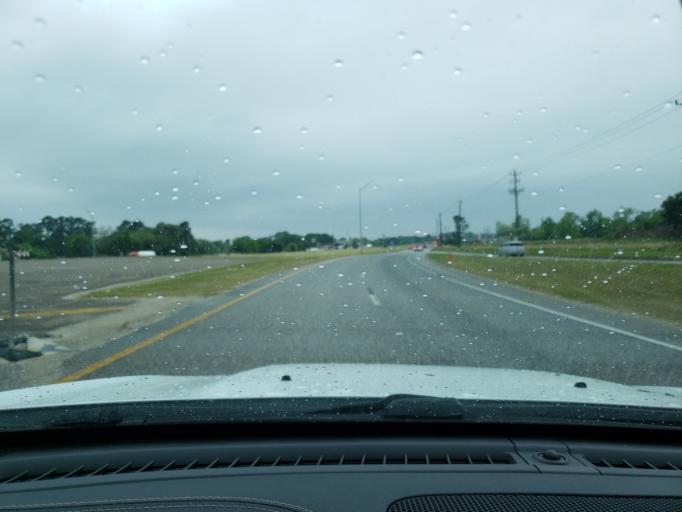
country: US
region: Texas
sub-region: Harris County
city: Baytown
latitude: 29.7615
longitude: -94.9243
